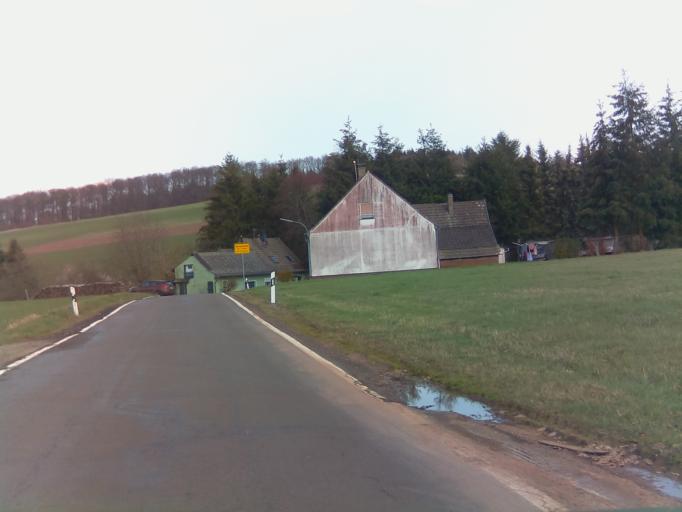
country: DE
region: Rheinland-Pfalz
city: Otzweiler
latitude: 49.7160
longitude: 7.5290
